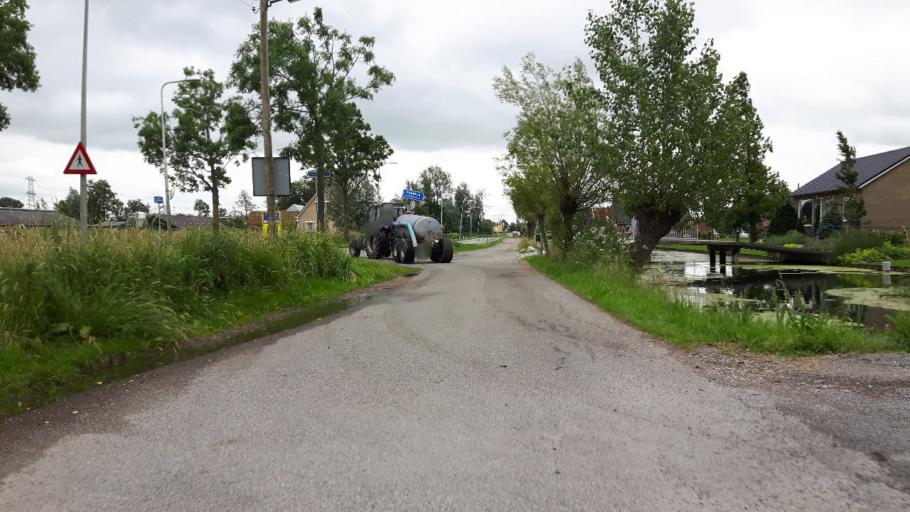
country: NL
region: Utrecht
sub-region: Gemeente Oudewater
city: Oudewater
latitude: 52.0494
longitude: 4.8499
